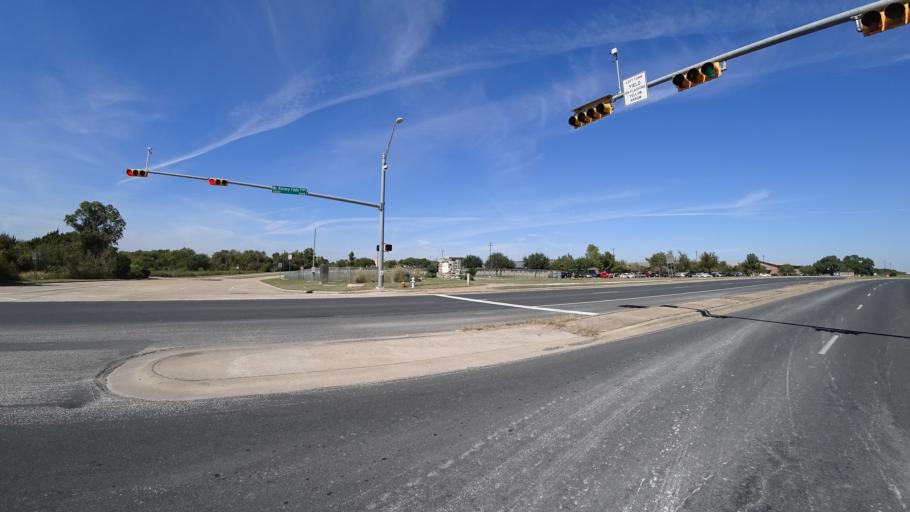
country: US
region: Texas
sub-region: Travis County
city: Austin
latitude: 30.1884
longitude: -97.7132
